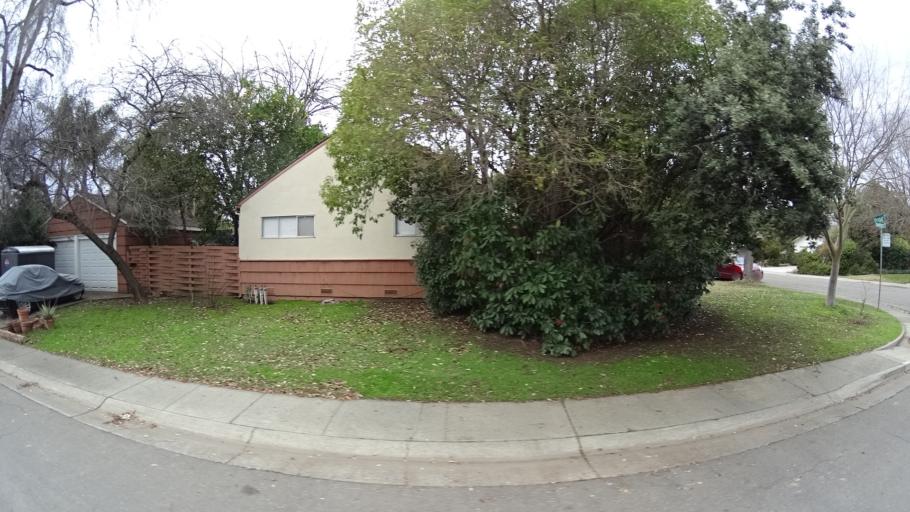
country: US
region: California
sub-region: Yolo County
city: Davis
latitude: 38.5504
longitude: -121.7618
